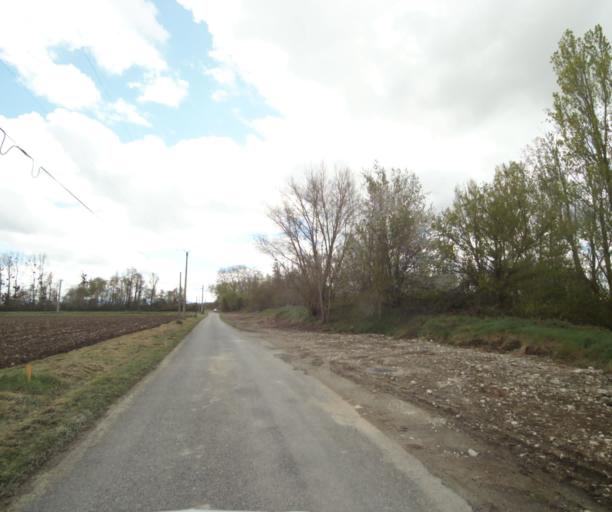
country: FR
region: Midi-Pyrenees
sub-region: Departement de l'Ariege
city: Saverdun
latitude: 43.2524
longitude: 1.5816
